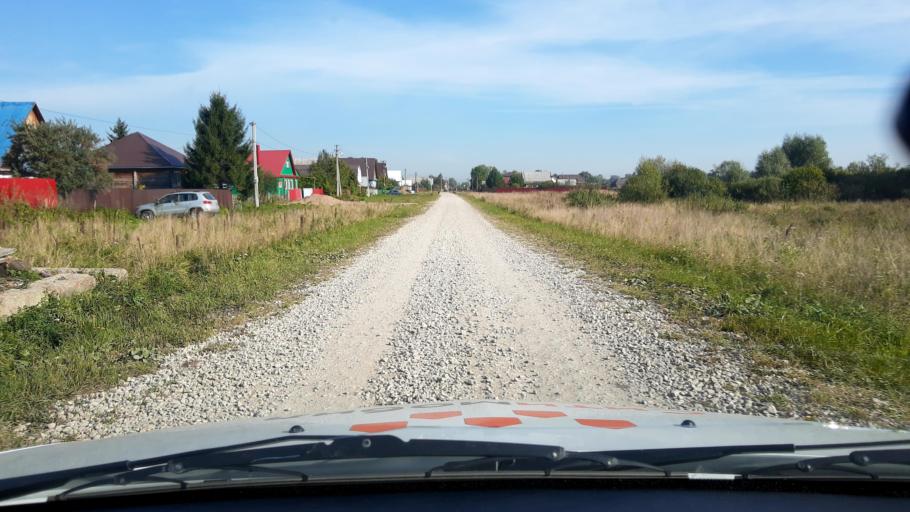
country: RU
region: Bashkortostan
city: Iglino
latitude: 54.8007
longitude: 56.3036
